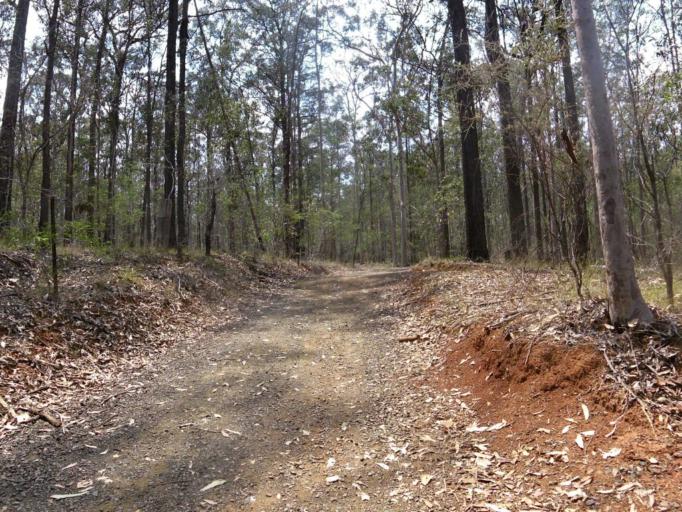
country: AU
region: Queensland
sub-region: Logan
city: Springwood
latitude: -27.6074
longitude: 153.1563
